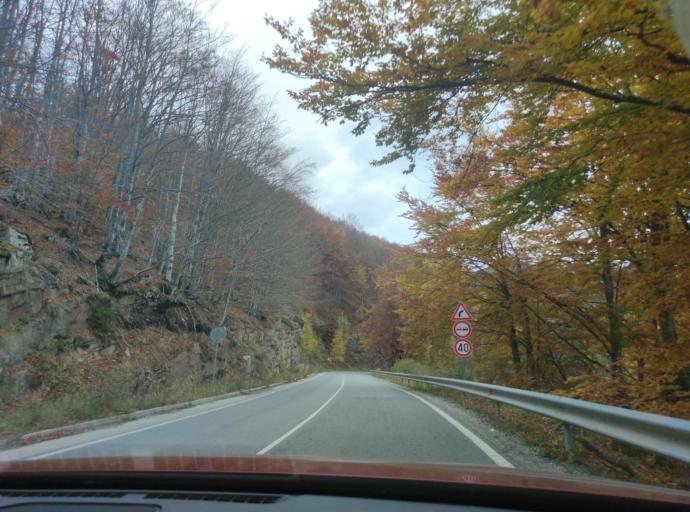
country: BG
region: Sofiya
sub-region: Obshtina Godech
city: Godech
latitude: 43.1083
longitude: 23.1052
